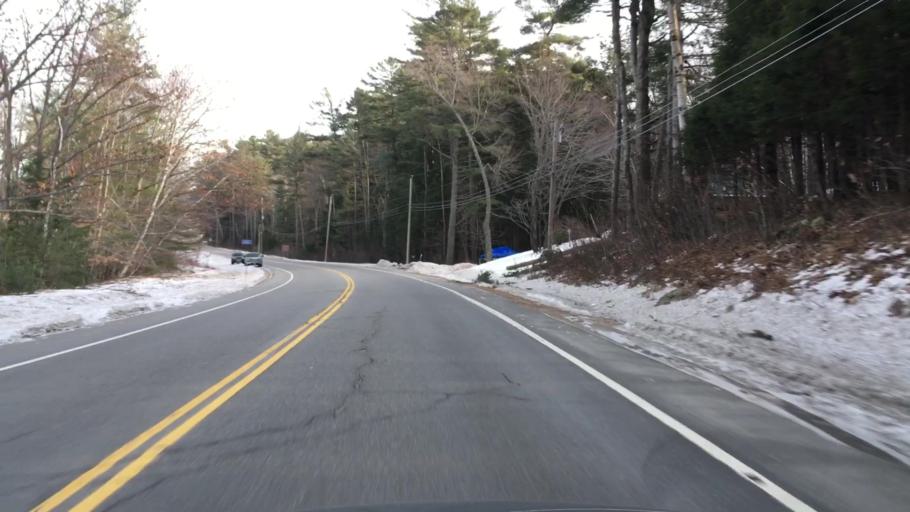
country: US
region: New Hampshire
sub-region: Sullivan County
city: Sunapee
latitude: 43.3416
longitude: -72.0805
